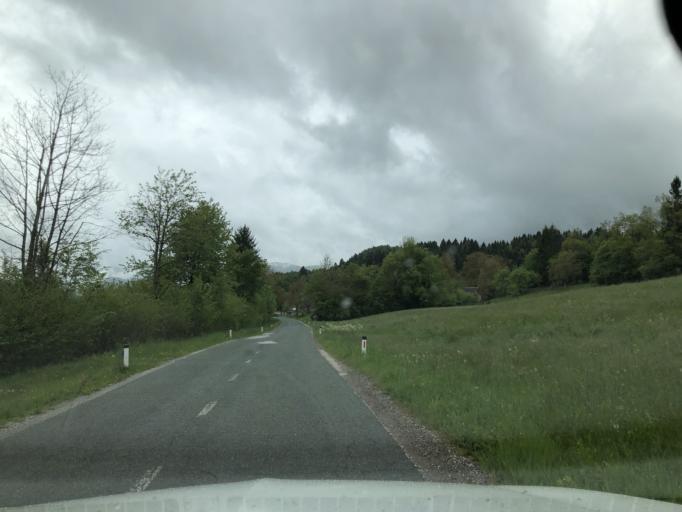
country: SI
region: Gorje
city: Zgornje Gorje
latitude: 46.3972
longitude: 14.0727
